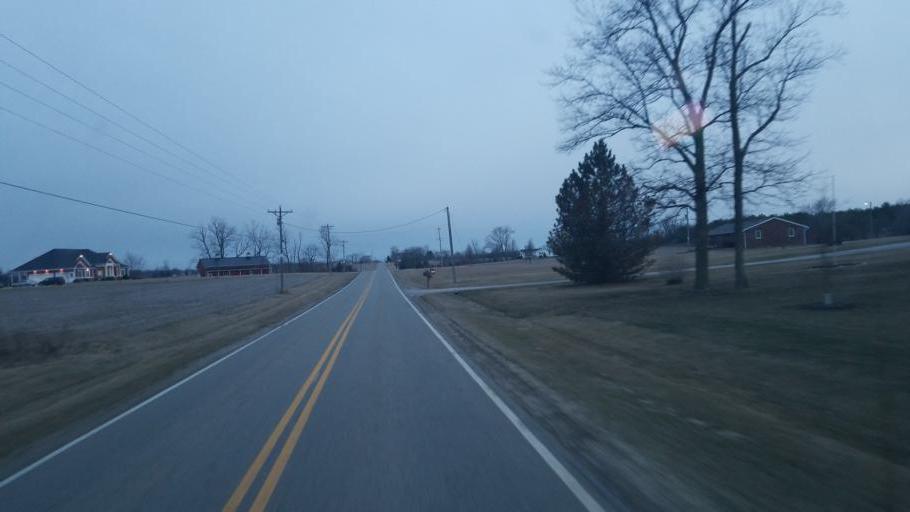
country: US
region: Ohio
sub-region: Defiance County
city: Hicksville
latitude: 41.3249
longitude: -84.7568
